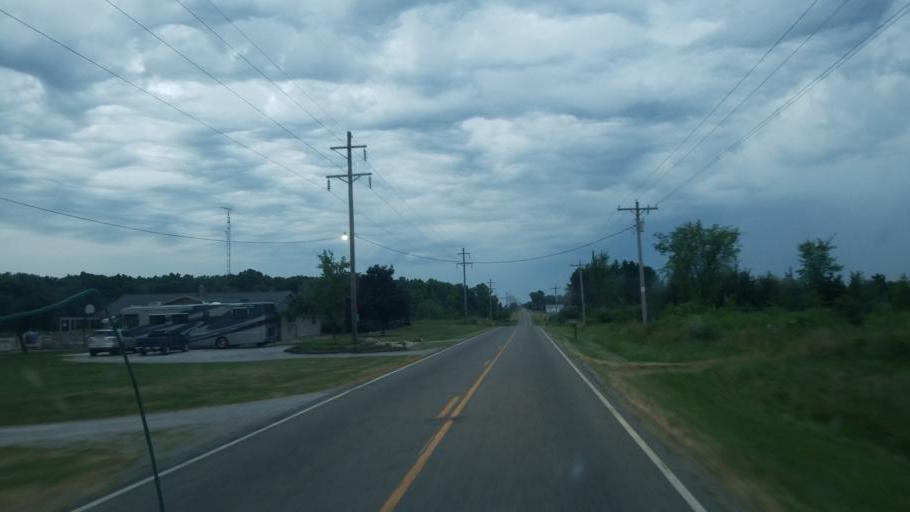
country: US
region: Ohio
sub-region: Defiance County
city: Hicksville
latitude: 41.3646
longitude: -84.7671
